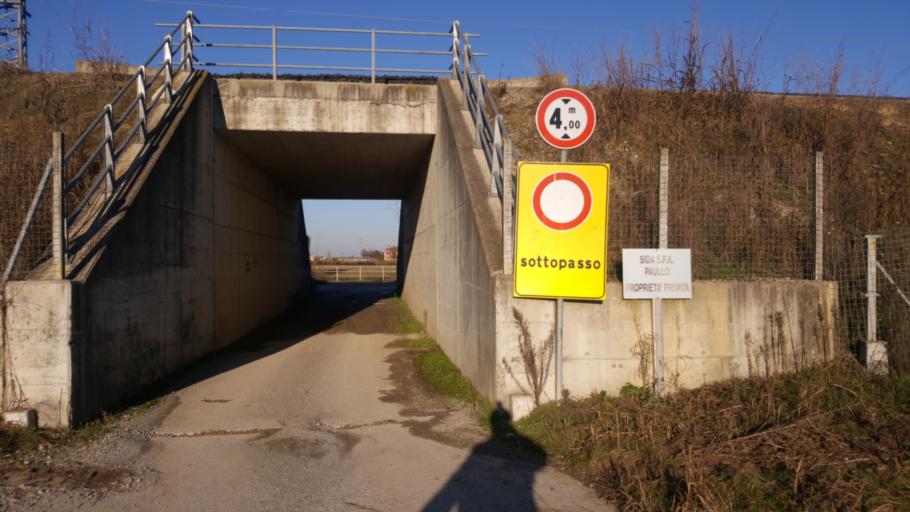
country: IT
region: Emilia-Romagna
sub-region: Provincia di Piacenza
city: Roveleto
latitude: 44.9707
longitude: 9.8921
